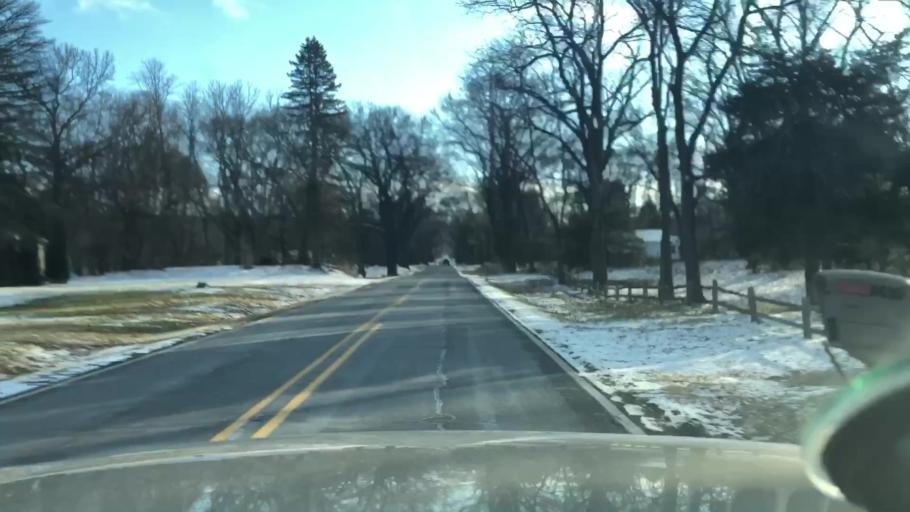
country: US
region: Michigan
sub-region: Jackson County
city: Vandercook Lake
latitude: 42.1534
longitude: -84.4521
